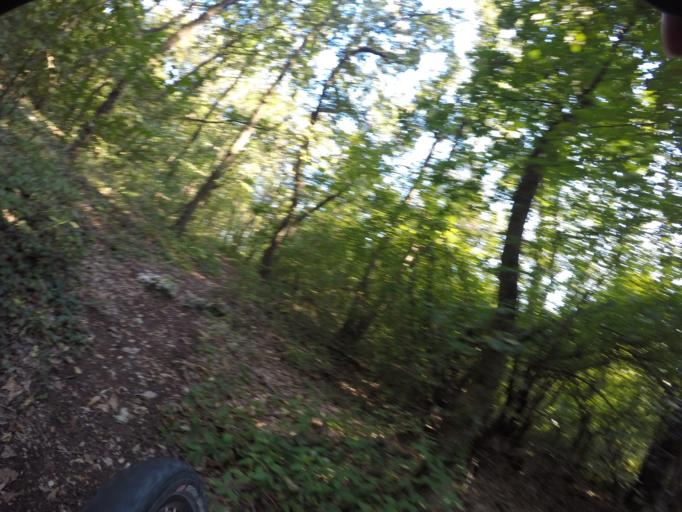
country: AT
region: Lower Austria
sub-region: Politischer Bezirk Bruck an der Leitha
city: Mannersdorf am Leithagebirge
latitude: 47.9643
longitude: 16.6015
